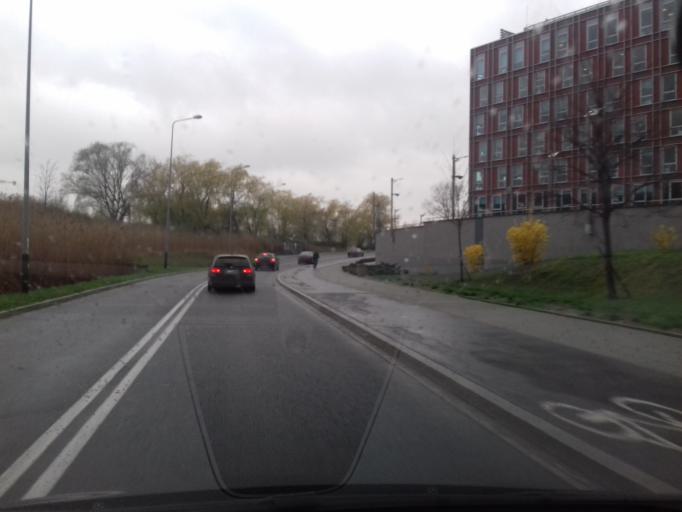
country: PL
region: Lesser Poland Voivodeship
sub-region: Krakow
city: Krakow
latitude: 50.0256
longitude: 19.9507
